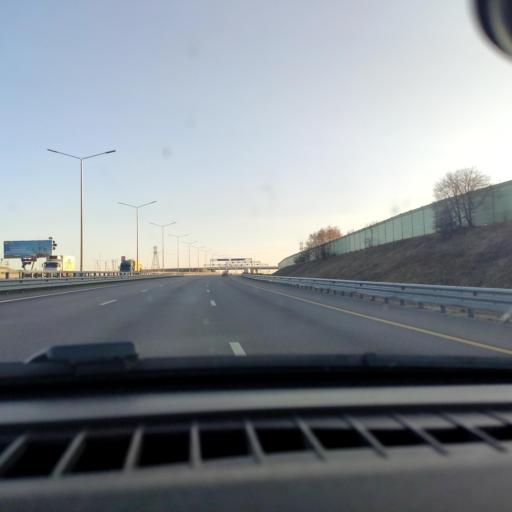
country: RU
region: Voronezj
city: Ramon'
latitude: 51.8265
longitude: 39.2476
